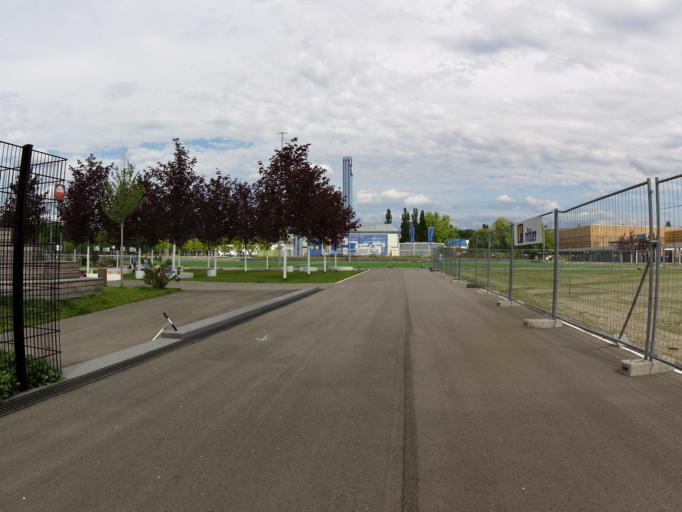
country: DE
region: Baden-Wuerttemberg
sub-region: Freiburg Region
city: Lahr
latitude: 48.3366
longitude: 7.8443
